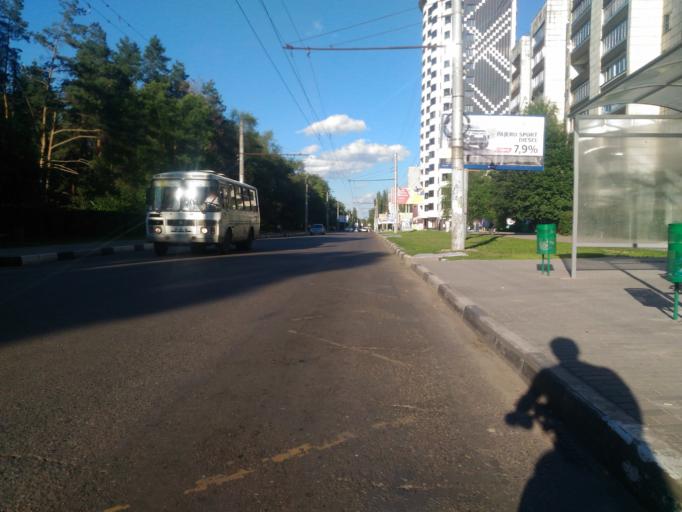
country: RU
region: Voronezj
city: Pridonskoy
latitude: 51.6516
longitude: 39.1231
